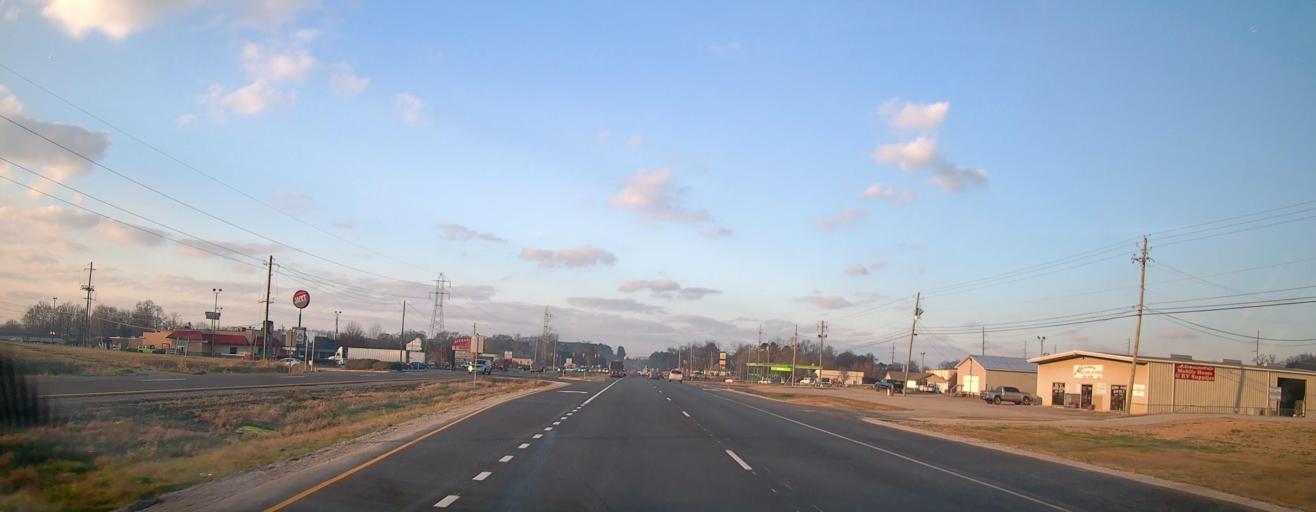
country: US
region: Alabama
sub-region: Calhoun County
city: Alexandria
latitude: 33.7802
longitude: -85.8958
